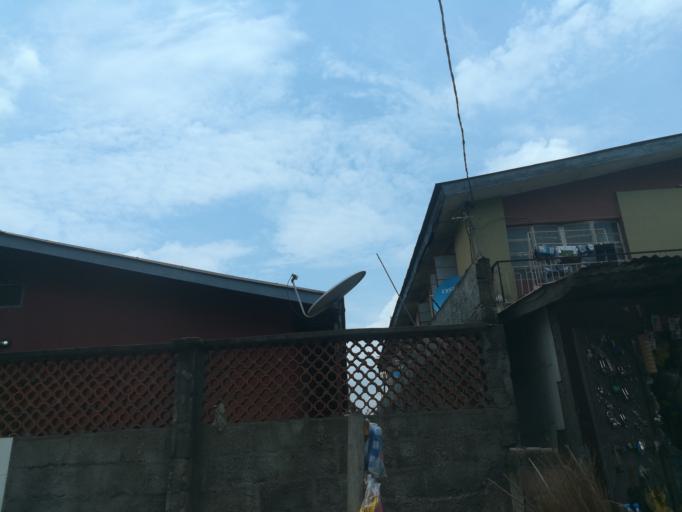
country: NG
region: Lagos
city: Ikeja
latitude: 6.5935
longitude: 3.3606
